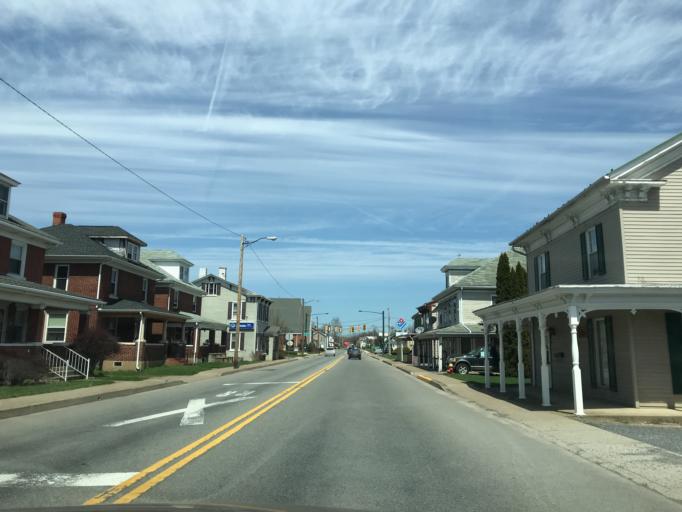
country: US
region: Pennsylvania
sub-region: Snyder County
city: Selinsgrove
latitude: 40.8028
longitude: -76.8604
